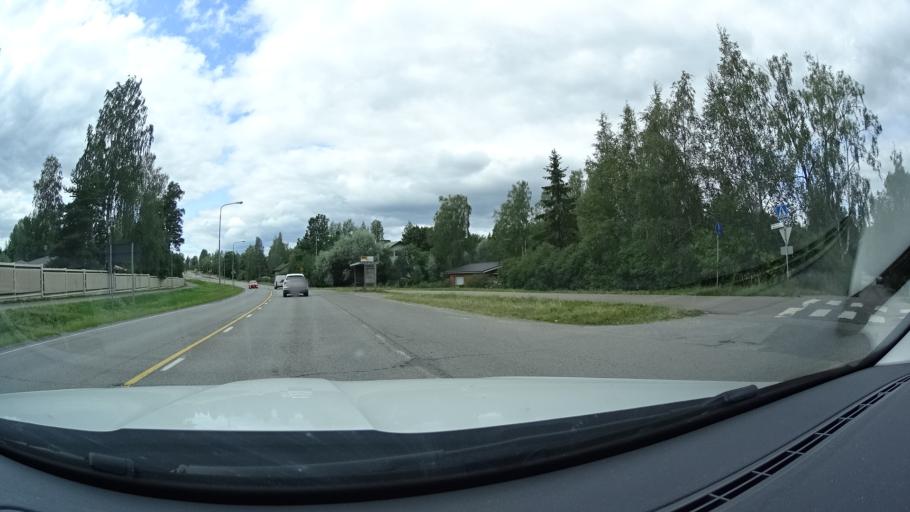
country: FI
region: Uusimaa
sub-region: Helsinki
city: Kerava
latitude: 60.3450
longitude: 25.0958
